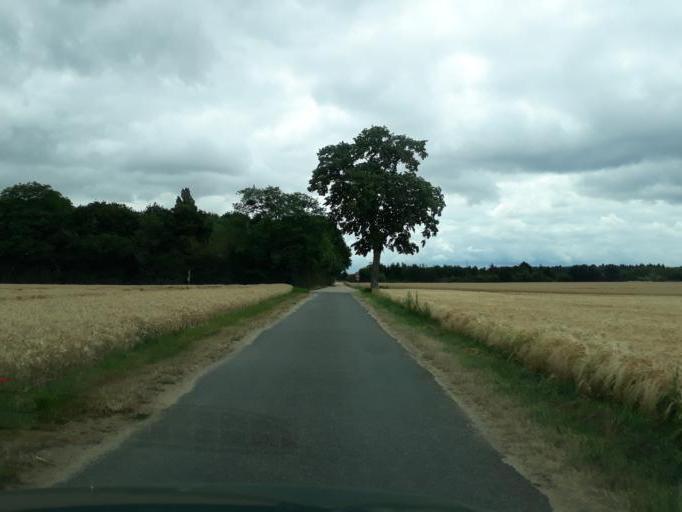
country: FR
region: Centre
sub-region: Departement du Loiret
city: Sandillon
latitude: 47.8427
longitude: 1.9990
